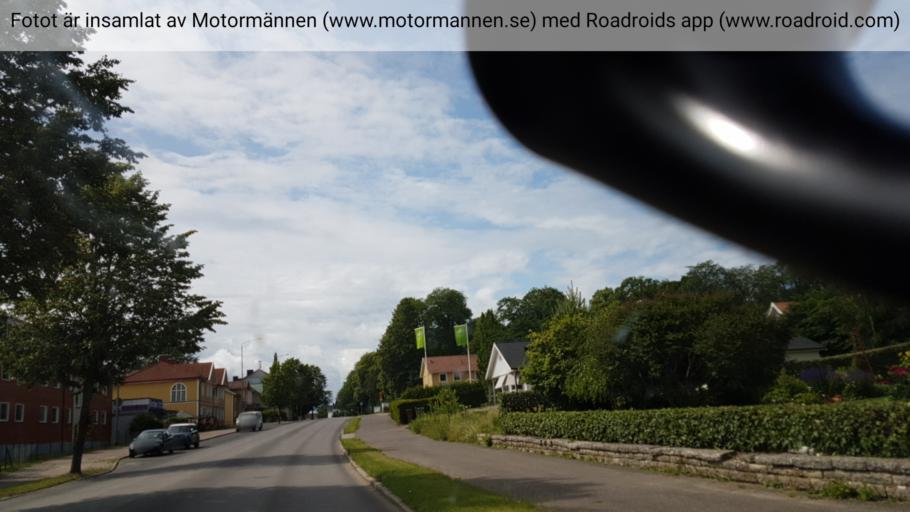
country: SE
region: Vaestra Goetaland
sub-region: Falkopings Kommun
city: Falkoeping
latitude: 58.1820
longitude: 13.5519
